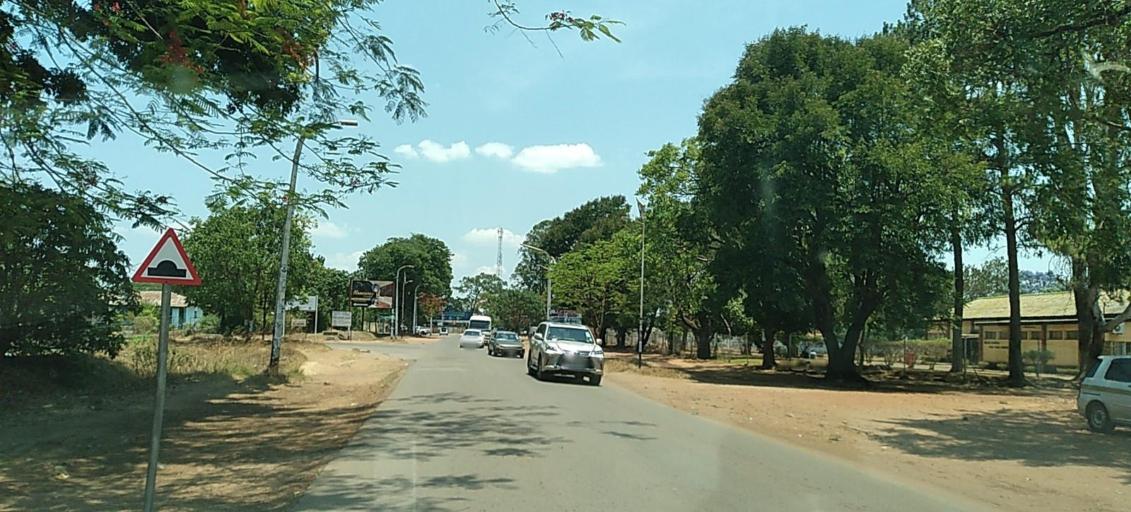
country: ZM
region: Copperbelt
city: Luanshya
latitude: -13.1371
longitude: 28.4201
